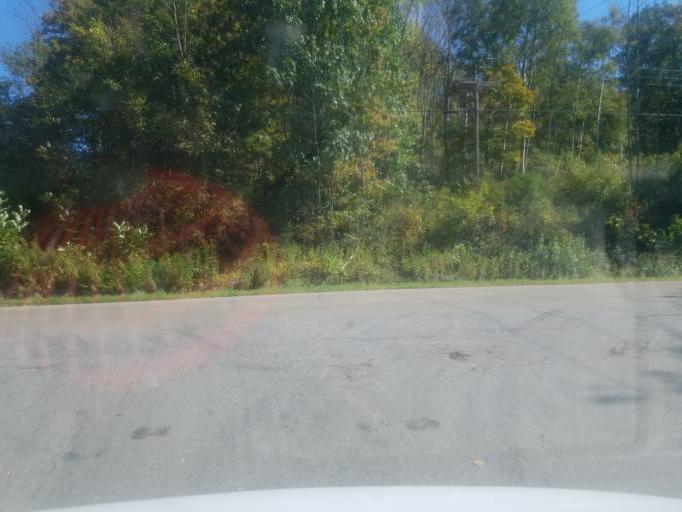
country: US
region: New York
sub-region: Allegany County
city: Friendship
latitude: 42.3148
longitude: -78.1069
